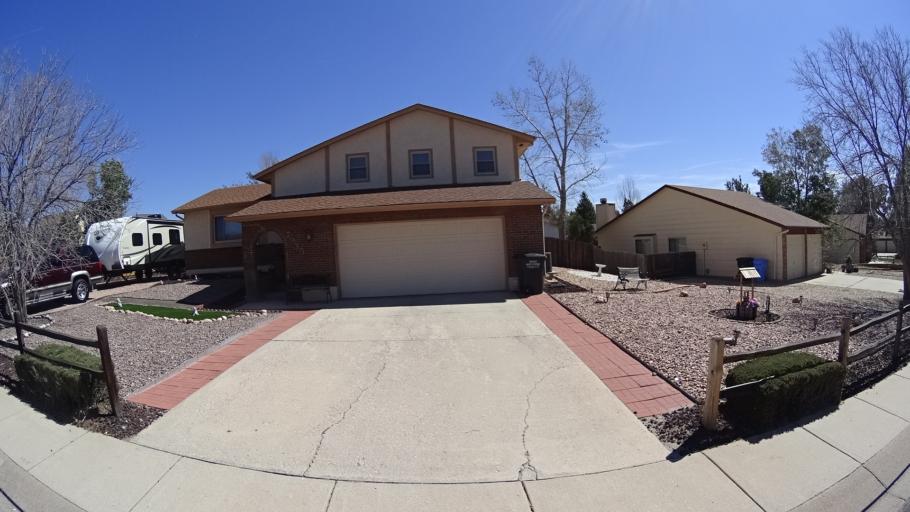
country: US
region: Colorado
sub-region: El Paso County
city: Black Forest
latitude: 38.9472
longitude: -104.7612
